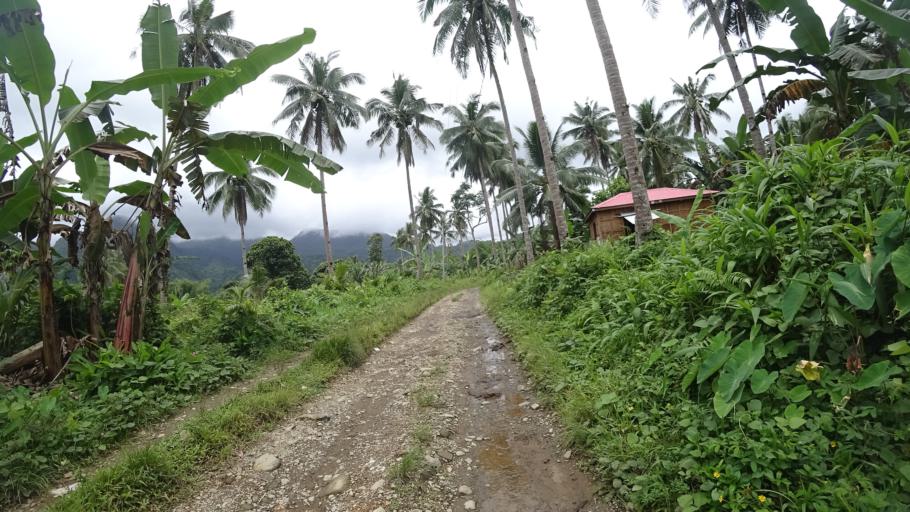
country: PH
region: Eastern Visayas
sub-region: Province of Leyte
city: Bugho
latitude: 10.8300
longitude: 124.8879
